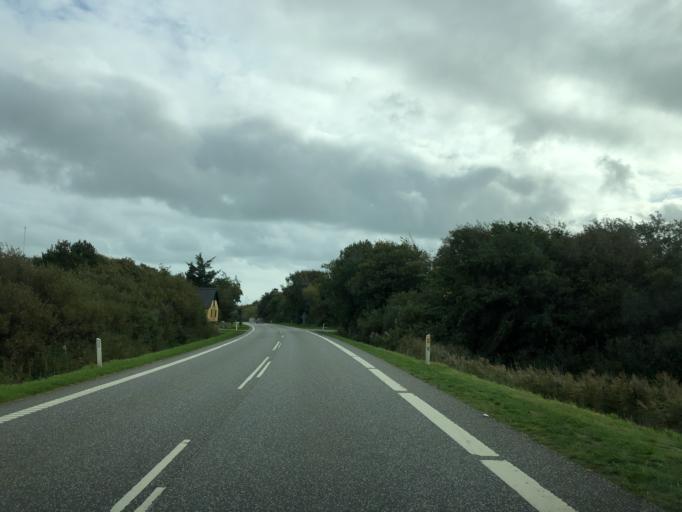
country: DK
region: North Denmark
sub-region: Thisted Kommune
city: Hurup
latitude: 56.6802
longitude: 8.3953
